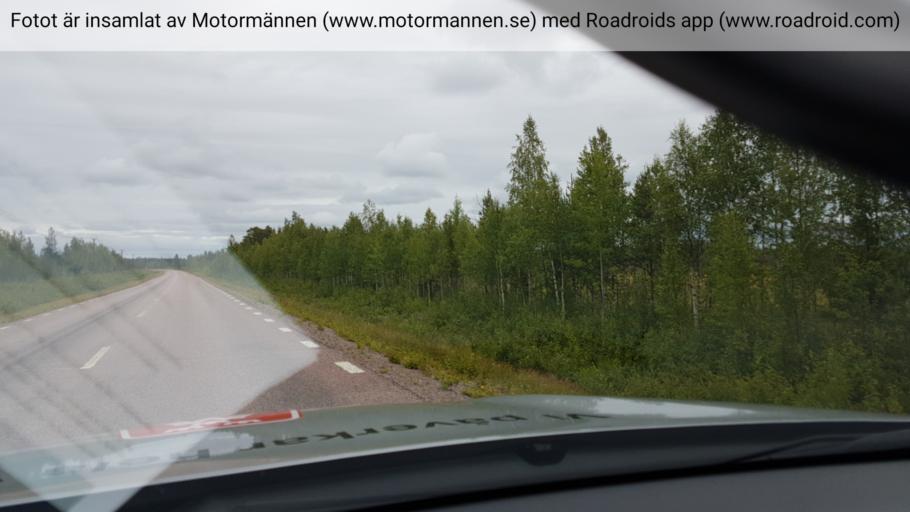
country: SE
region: Norrbotten
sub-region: Pajala Kommun
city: Pajala
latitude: 67.0988
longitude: 22.5831
